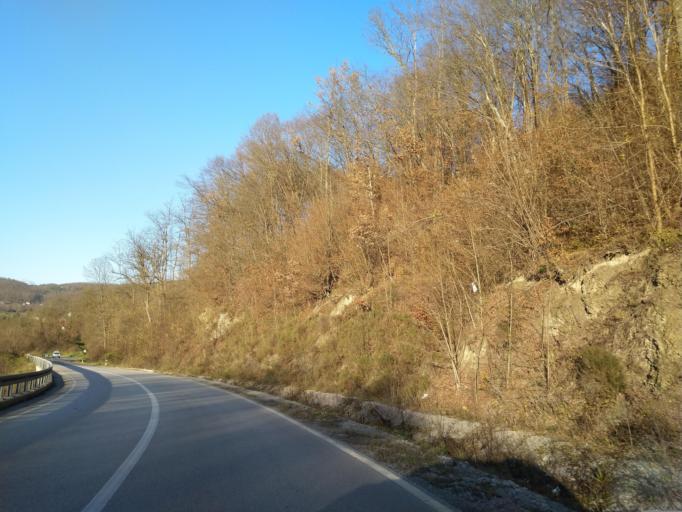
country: RS
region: Central Serbia
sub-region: Zlatiborski Okrug
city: Pozega
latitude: 43.9230
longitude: 19.9919
